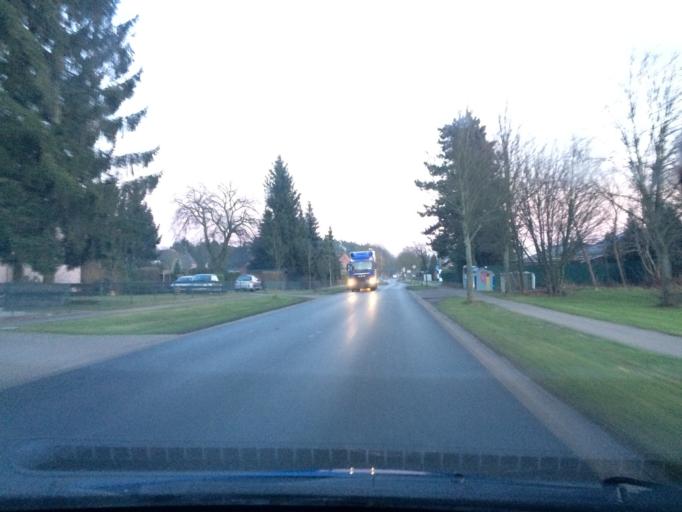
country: DE
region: Lower Saxony
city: Embsen
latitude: 53.1806
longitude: 10.3587
